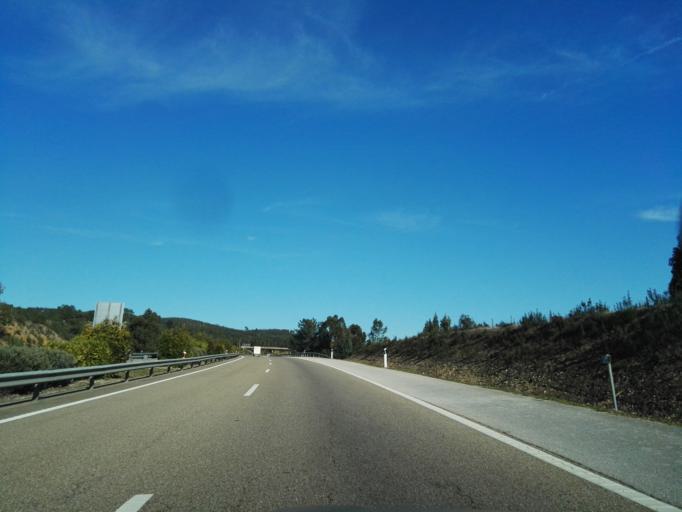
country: PT
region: Santarem
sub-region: Constancia
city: Constancia
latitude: 39.4888
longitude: -8.3133
